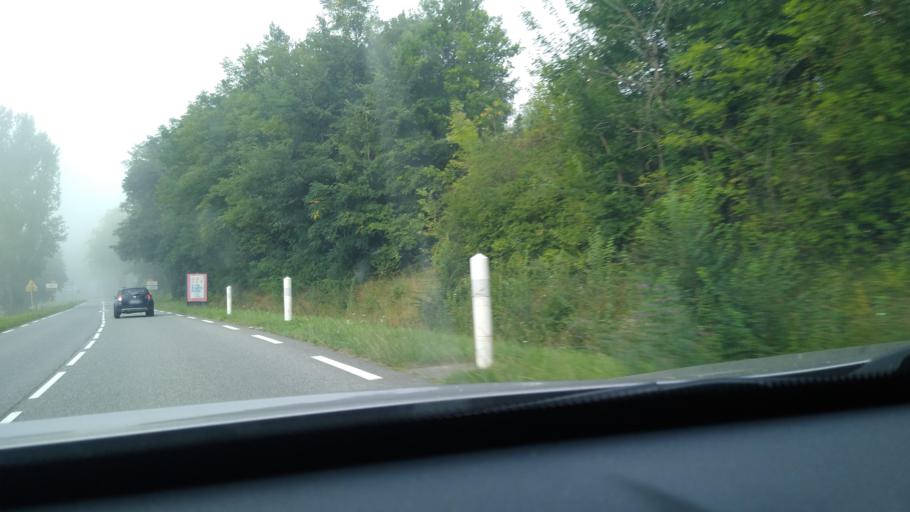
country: FR
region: Midi-Pyrenees
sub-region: Departement de la Haute-Garonne
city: Salies-du-Salat
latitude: 43.0949
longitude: 0.9522
